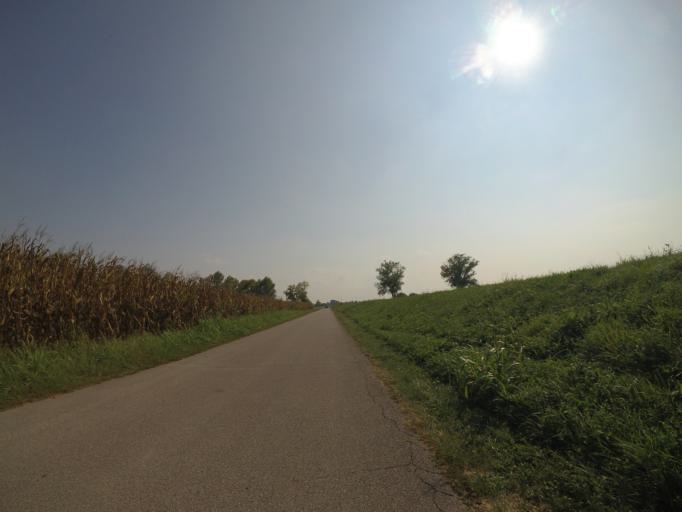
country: IT
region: Friuli Venezia Giulia
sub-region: Provincia di Udine
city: Camino al Tagliamento
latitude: 45.9225
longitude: 12.9250
